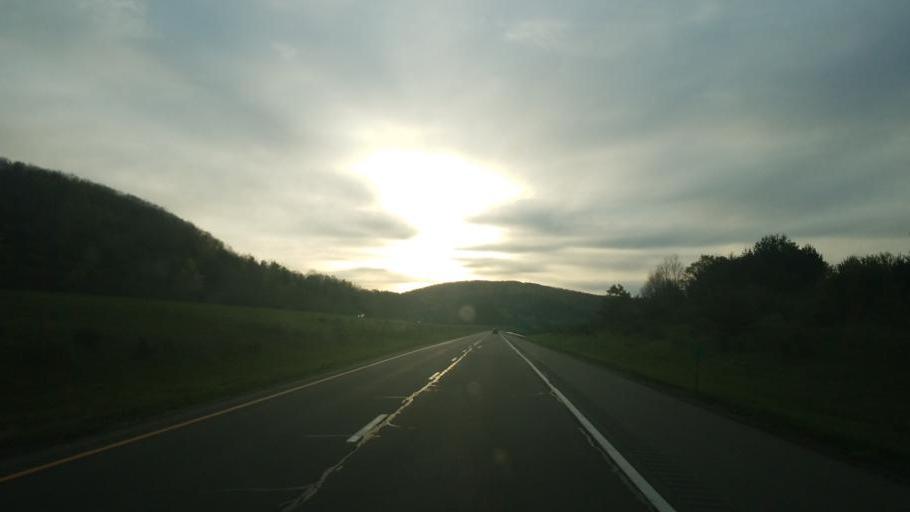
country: US
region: New York
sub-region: Allegany County
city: Cuba
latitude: 42.2251
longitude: -78.2610
